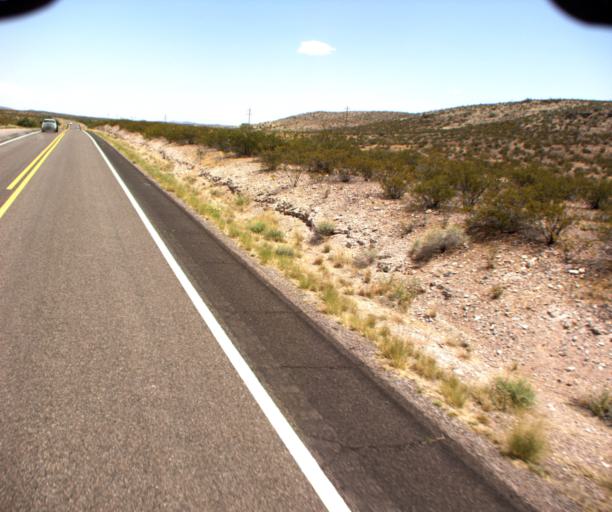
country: US
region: Arizona
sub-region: Graham County
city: Swift Trail Junction
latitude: 32.7517
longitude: -109.4062
